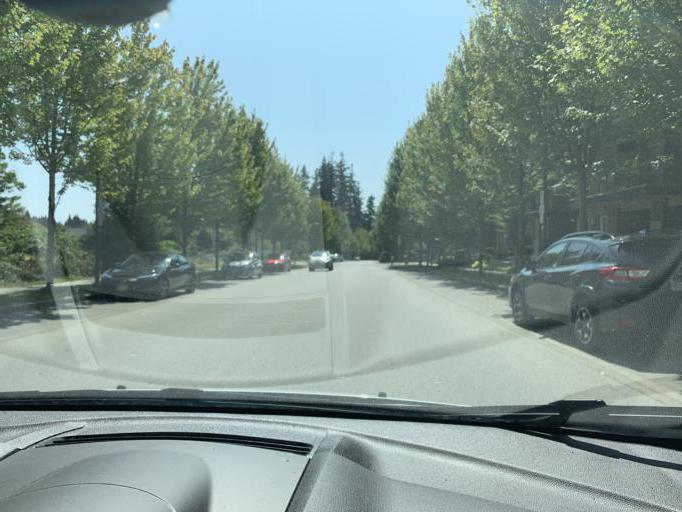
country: CA
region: British Columbia
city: West End
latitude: 49.2520
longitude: -123.2334
